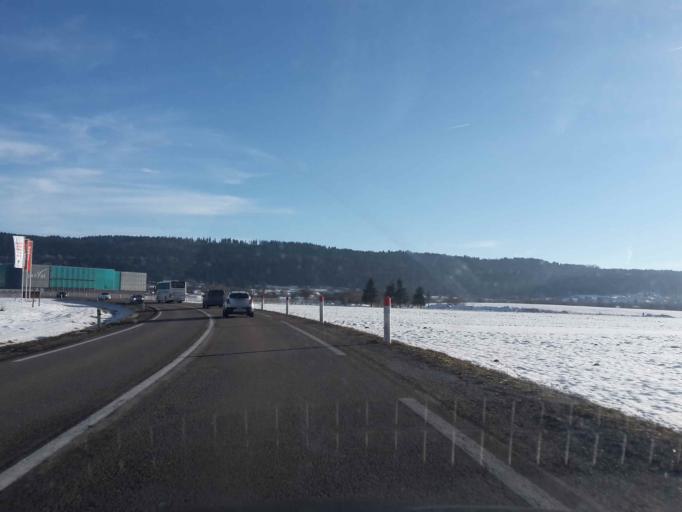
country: FR
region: Franche-Comte
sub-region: Departement du Doubs
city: Pontarlier
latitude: 46.9022
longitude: 6.3297
